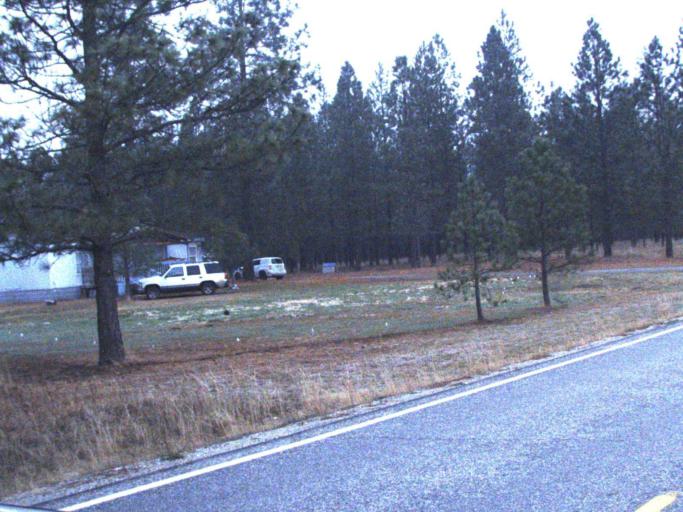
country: CA
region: British Columbia
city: Grand Forks
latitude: 48.9919
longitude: -118.2254
